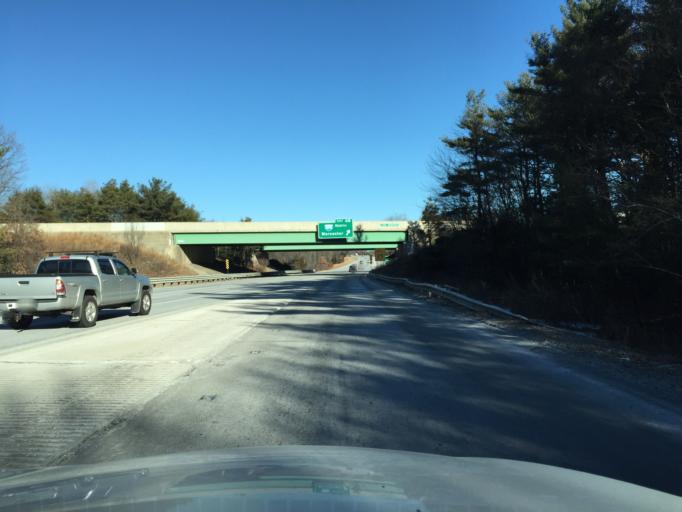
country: US
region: Massachusetts
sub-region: Bristol County
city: Mansfield
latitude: 42.0255
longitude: -71.2579
